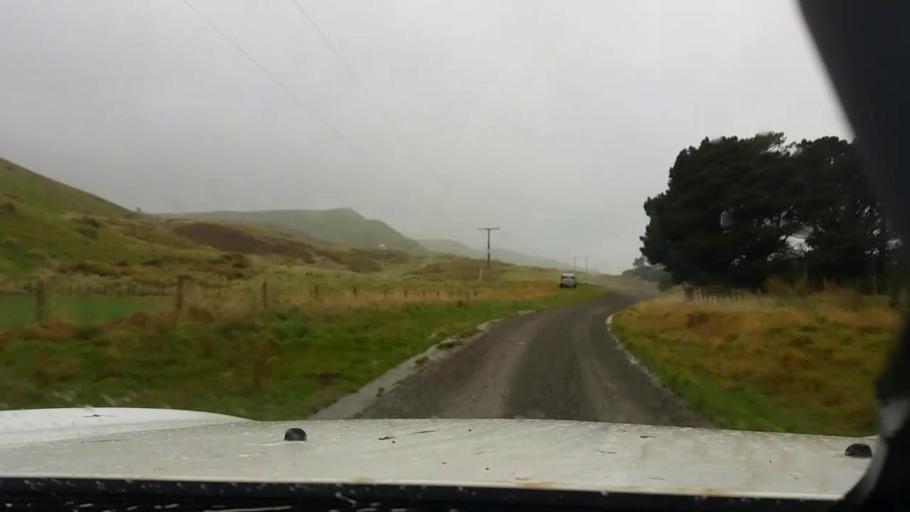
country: NZ
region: Wellington
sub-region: Masterton District
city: Masterton
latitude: -41.2536
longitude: 175.9116
